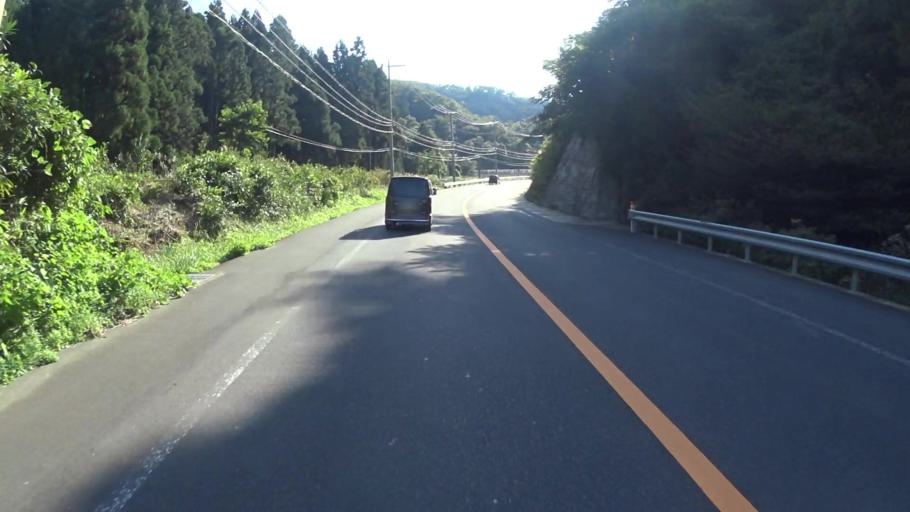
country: JP
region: Kyoto
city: Miyazu
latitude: 35.6602
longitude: 135.0080
